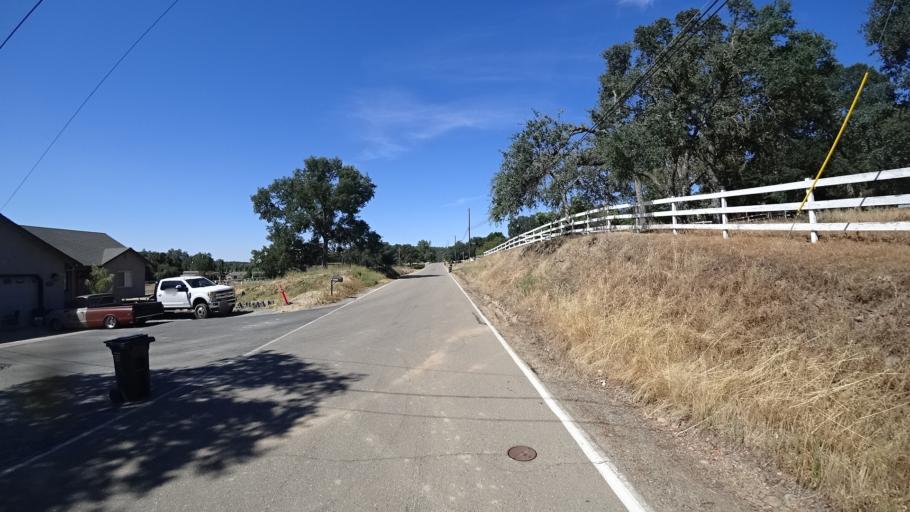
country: US
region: California
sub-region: Calaveras County
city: Rancho Calaveras
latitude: 38.1471
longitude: -120.8629
